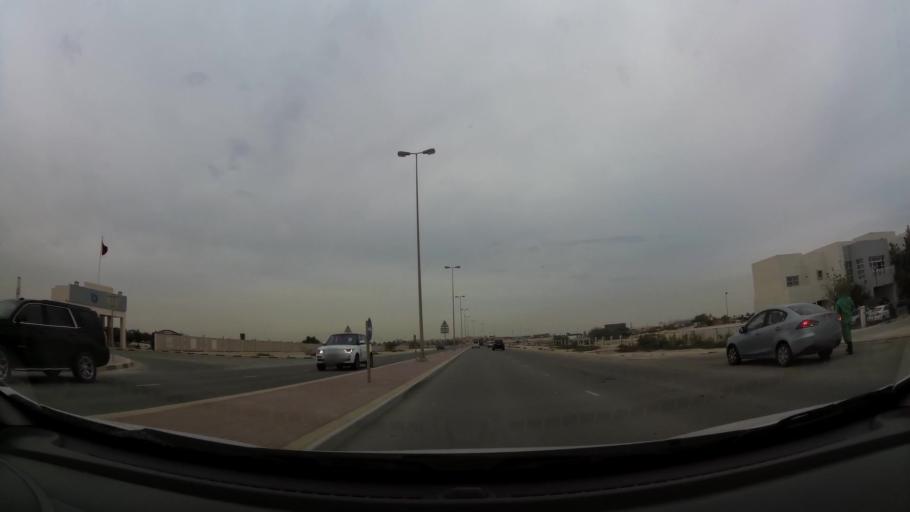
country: BH
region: Northern
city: Ar Rifa'
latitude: 26.0966
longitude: 50.5568
